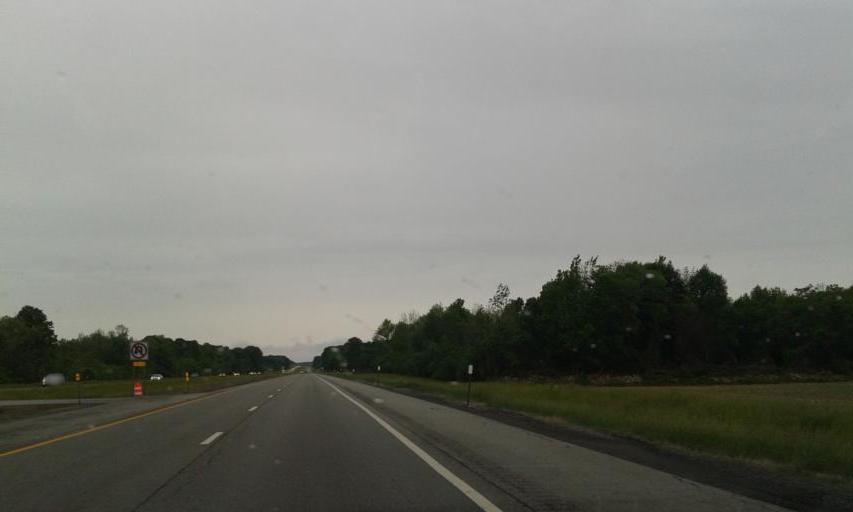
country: US
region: New York
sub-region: Genesee County
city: Le Roy
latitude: 43.0291
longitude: -77.9731
